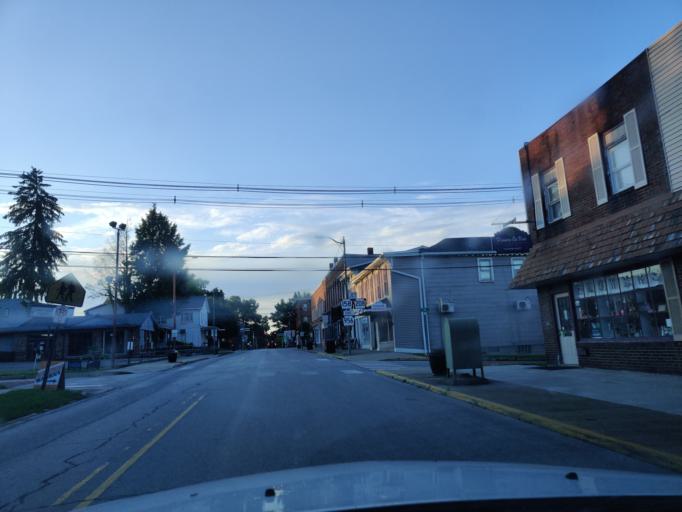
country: US
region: Pennsylvania
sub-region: Lawrence County
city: New Wilmington
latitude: 41.1211
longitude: -80.3331
